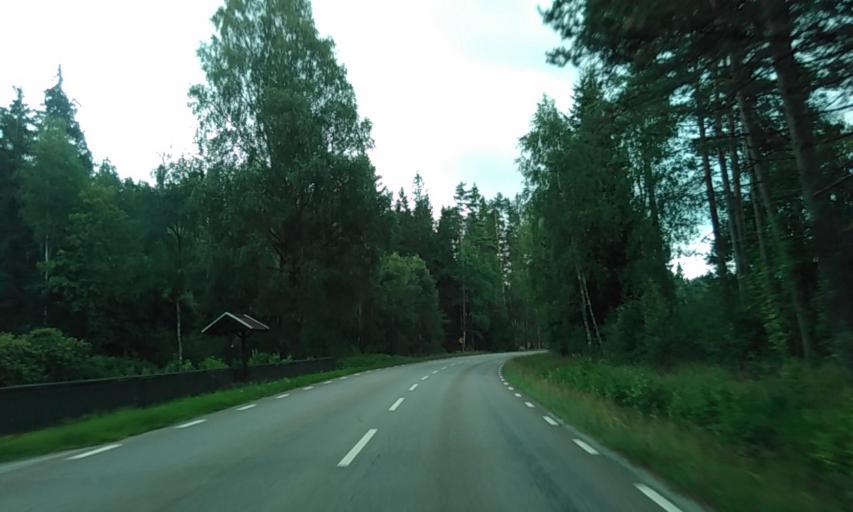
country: SE
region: Vaestra Goetaland
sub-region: Bollebygds Kommun
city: Bollebygd
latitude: 57.7085
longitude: 12.5825
